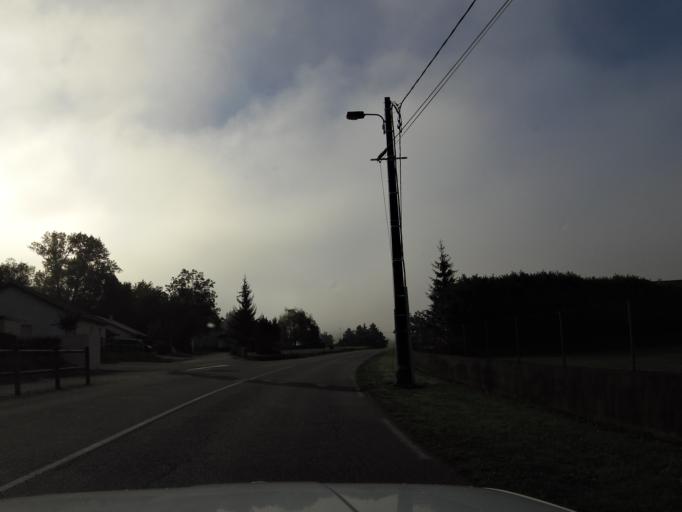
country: FR
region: Rhone-Alpes
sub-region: Departement de l'Isere
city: Bouvesse-Quirieu
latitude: 45.7987
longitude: 5.4581
